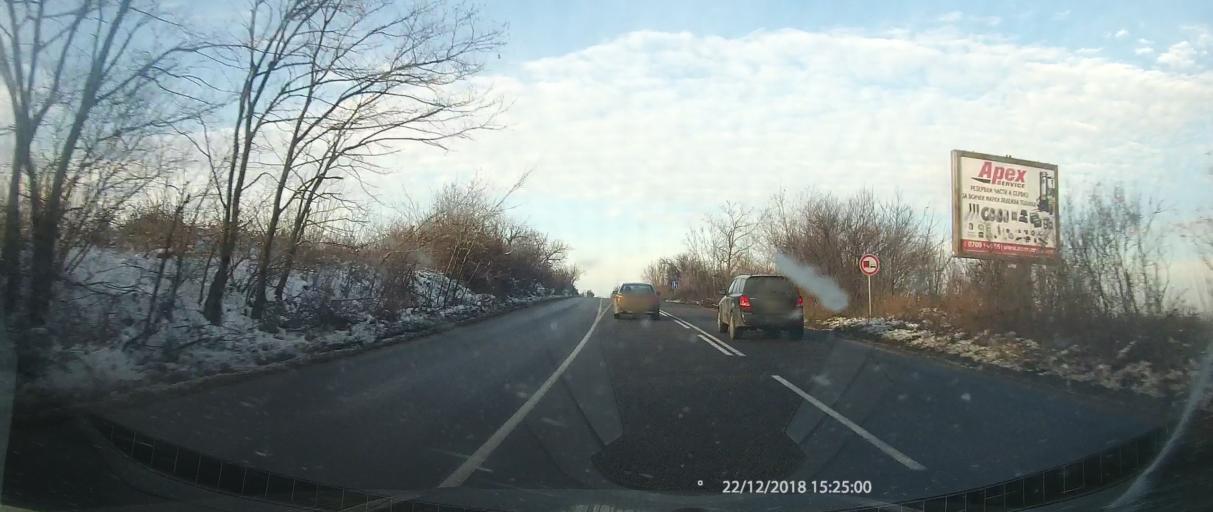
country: BG
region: Ruse
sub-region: Obshtina Ivanovo
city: Ivanovo
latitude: 43.7500
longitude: 25.9101
